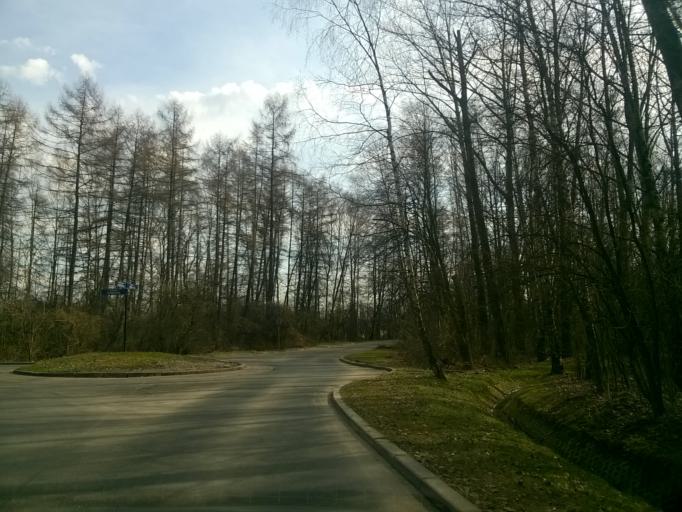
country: PL
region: Lesser Poland Voivodeship
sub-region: Powiat krakowski
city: Rzaska
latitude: 50.0920
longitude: 19.8655
